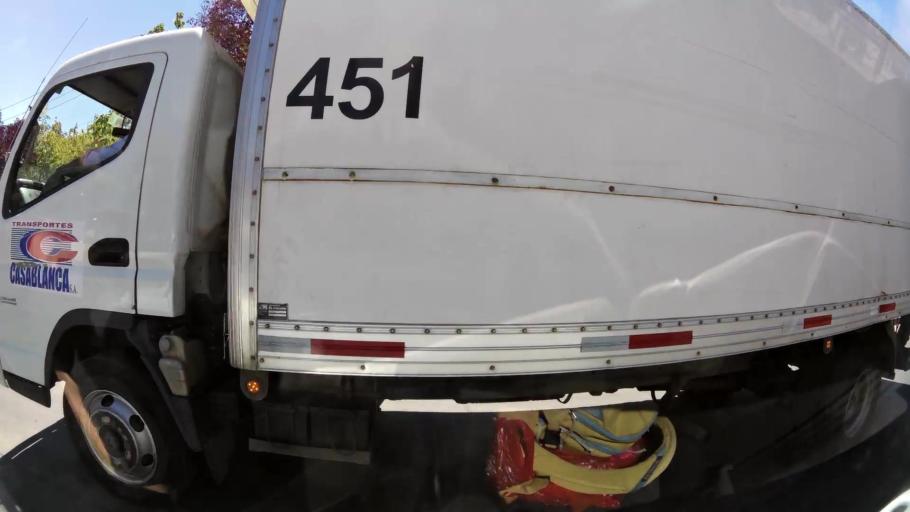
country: CL
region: O'Higgins
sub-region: Provincia de Cachapoal
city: Rancagua
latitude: -34.1597
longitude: -70.7170
